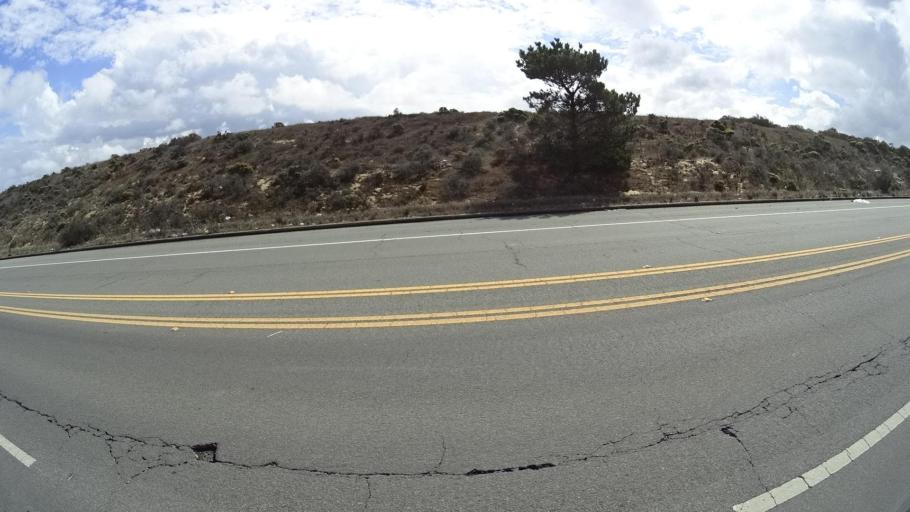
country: US
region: California
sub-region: Monterey County
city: Marina
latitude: 36.6725
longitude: -121.7613
